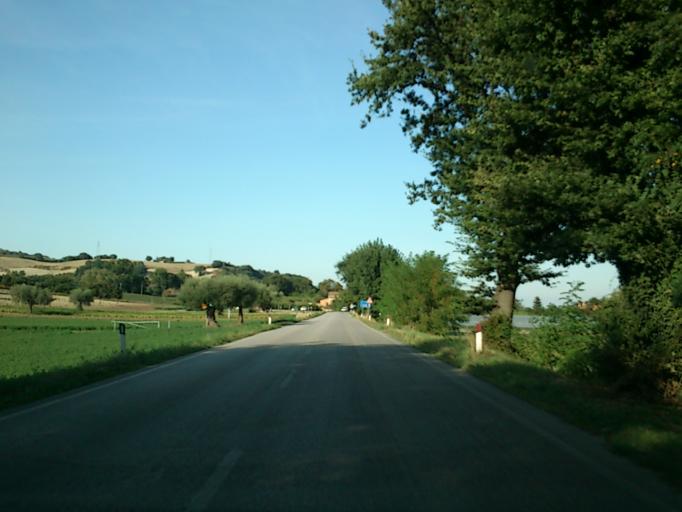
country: IT
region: The Marches
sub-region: Provincia di Pesaro e Urbino
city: Tavernelle
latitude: 43.7231
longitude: 12.8694
